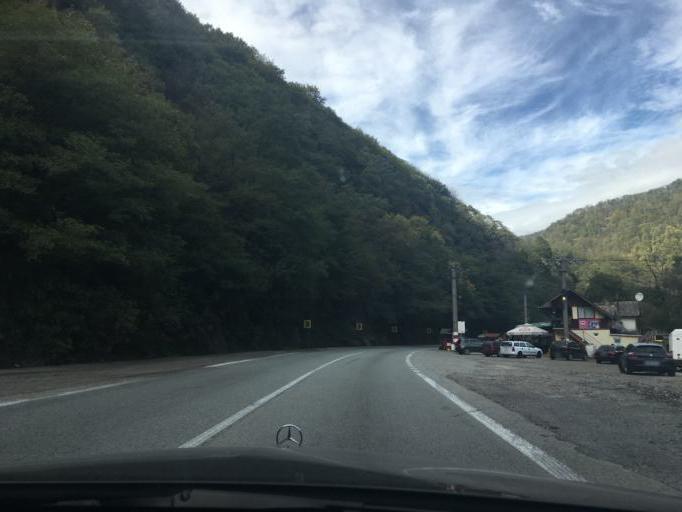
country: RO
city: Cainenii Mici
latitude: 45.5427
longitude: 24.2672
